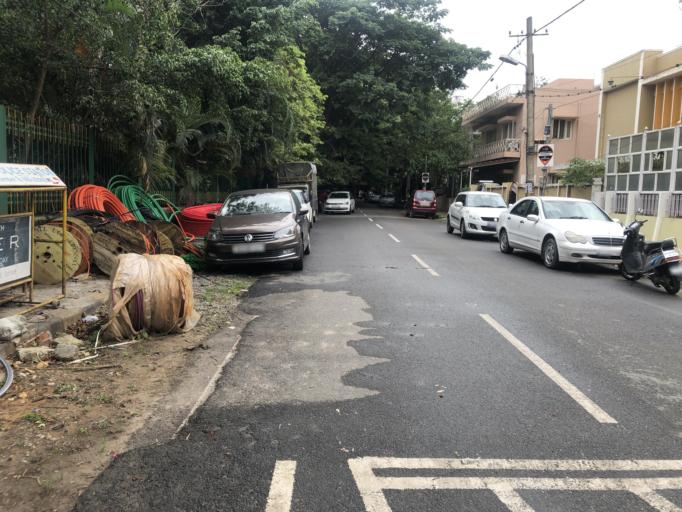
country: IN
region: Karnataka
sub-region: Bangalore Urban
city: Bangalore
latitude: 12.9253
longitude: 77.5827
